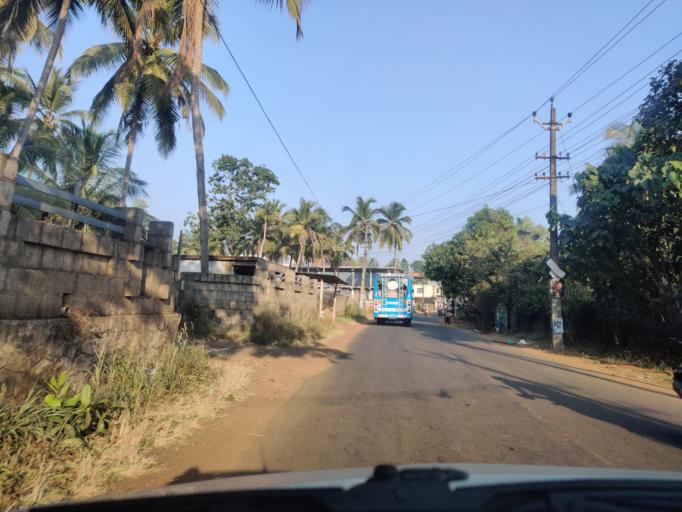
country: IN
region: Kerala
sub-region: Thrissur District
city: Kunnamkulam
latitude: 10.7349
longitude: 76.0247
